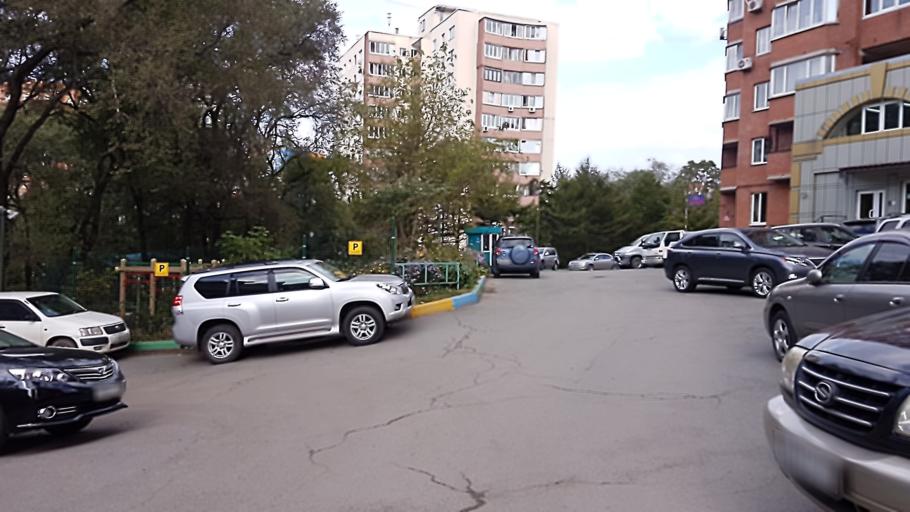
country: RU
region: Primorskiy
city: Vladivostok
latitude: 43.1293
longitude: 131.9094
